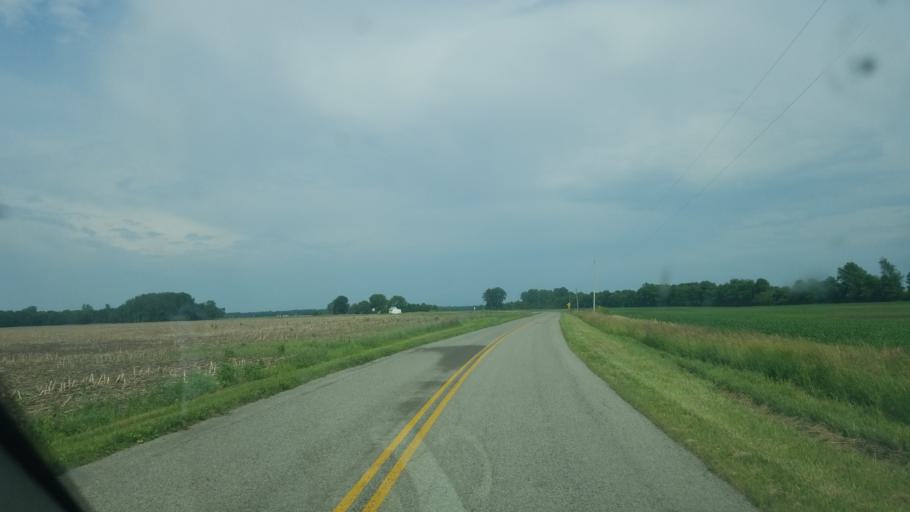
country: US
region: Ohio
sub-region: Champaign County
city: North Lewisburg
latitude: 40.1768
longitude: -83.4870
